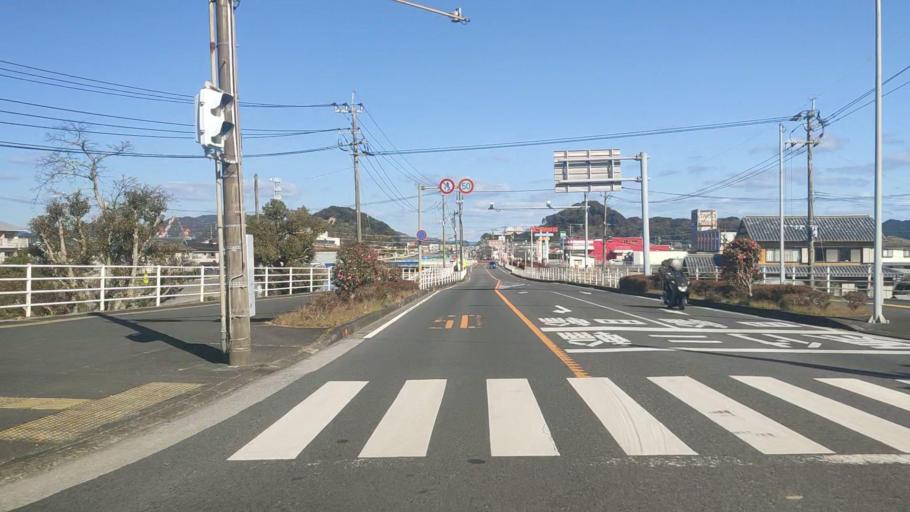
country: JP
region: Oita
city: Saiki
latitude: 32.9500
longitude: 131.9041
